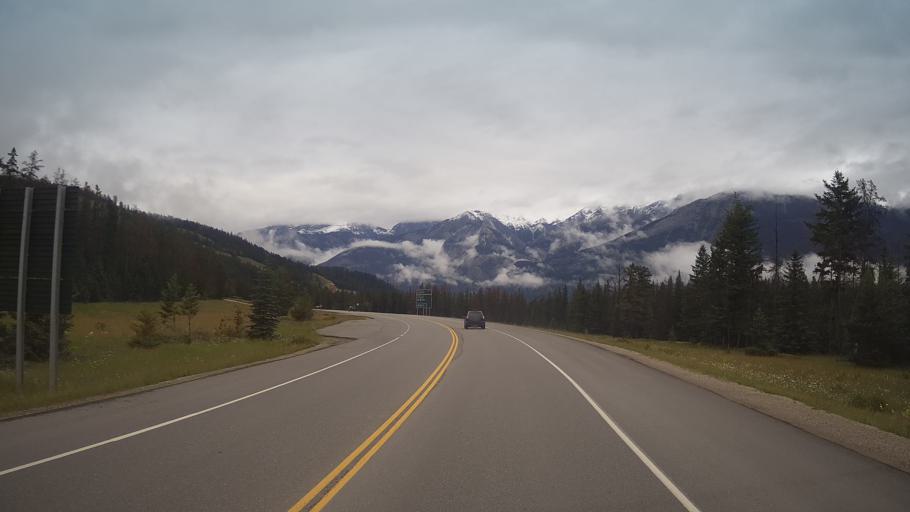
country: CA
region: Alberta
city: Jasper Park Lodge
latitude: 52.8970
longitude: -118.0674
